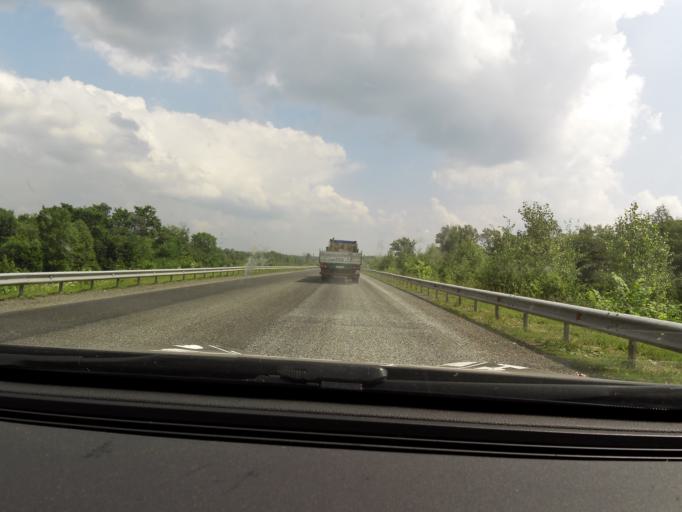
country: RU
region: Sverdlovsk
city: Ufimskiy
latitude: 56.7675
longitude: 58.1313
